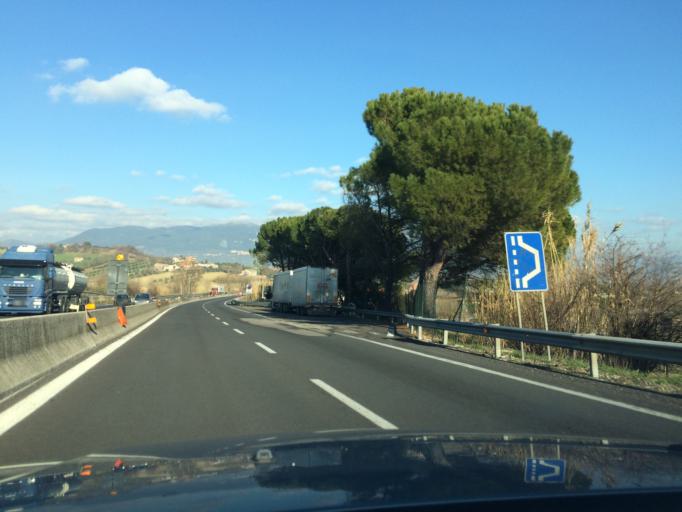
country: IT
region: Umbria
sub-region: Provincia di Terni
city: Narni Scalo
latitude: 42.5462
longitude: 12.5209
